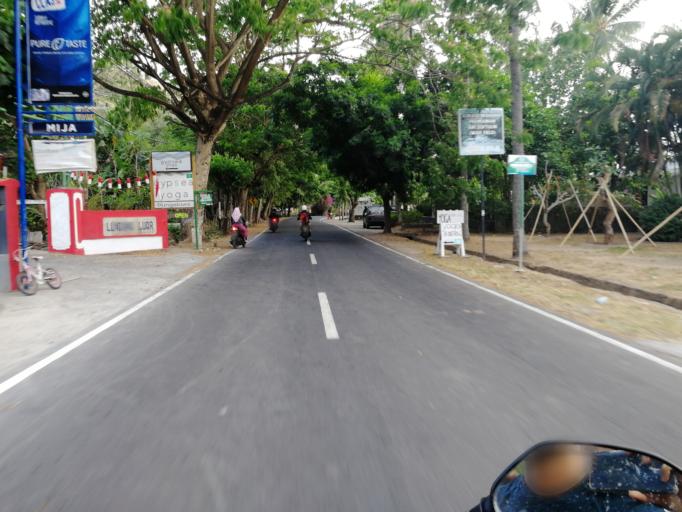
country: ID
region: West Nusa Tenggara
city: Karangsubagan
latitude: -8.4575
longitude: 116.0390
